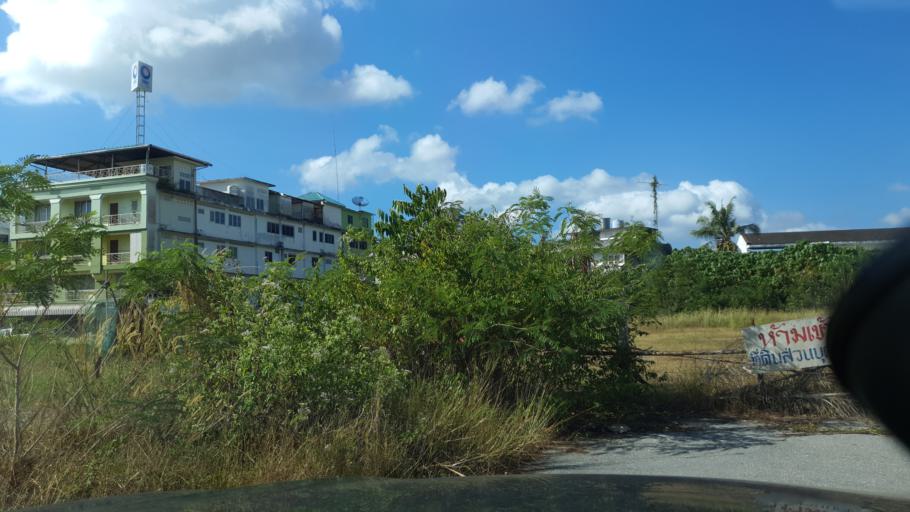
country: TH
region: Krabi
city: Krabi
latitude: 8.0679
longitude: 98.9156
